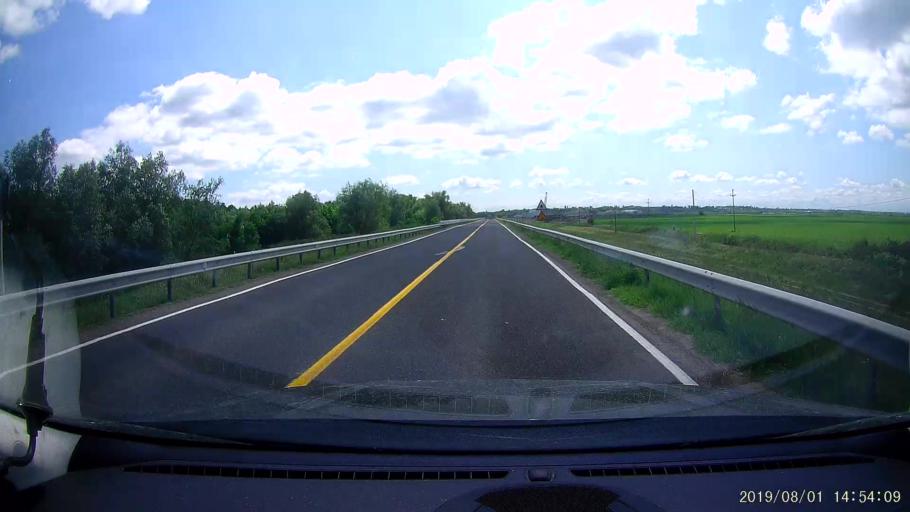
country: RO
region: Braila
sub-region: Municipiul Braila
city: Braila
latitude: 45.3224
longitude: 27.9936
